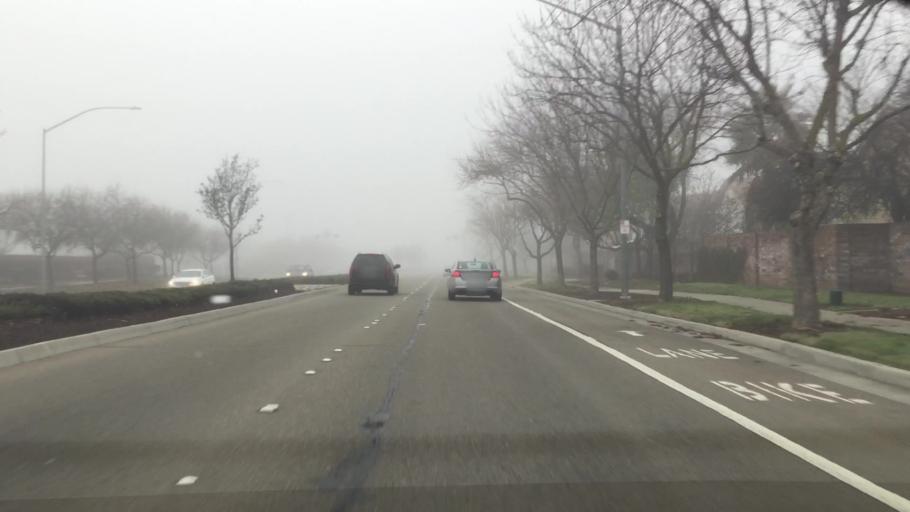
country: US
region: California
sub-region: San Joaquin County
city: Tracy
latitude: 37.7542
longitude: -121.4489
